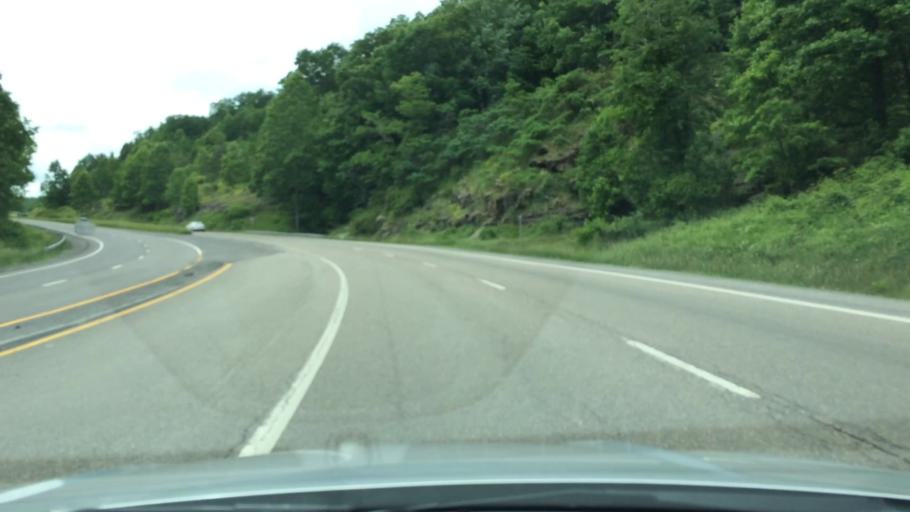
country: US
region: Kentucky
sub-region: Letcher County
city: Jenkins
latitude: 37.1575
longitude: -82.6181
